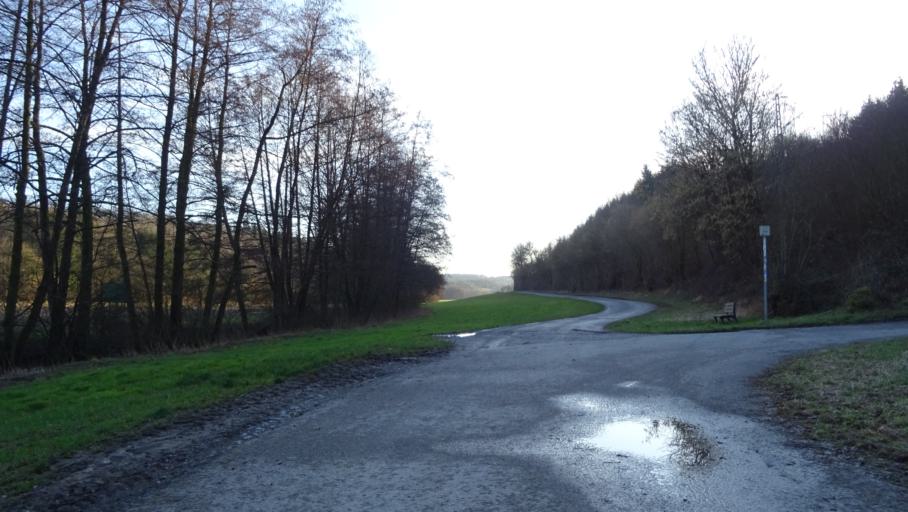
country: DE
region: Baden-Wuerttemberg
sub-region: Karlsruhe Region
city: Limbach
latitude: 49.4118
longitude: 9.2368
